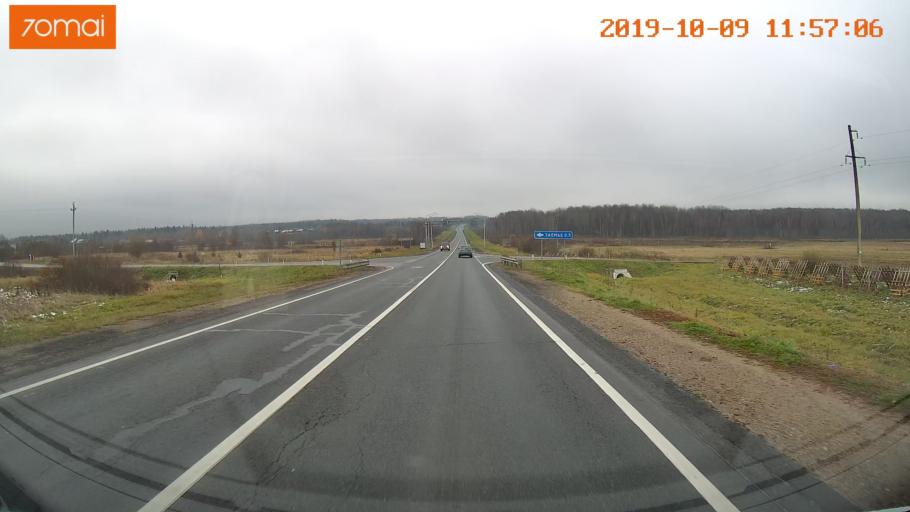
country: RU
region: Vologda
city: Gryazovets
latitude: 58.7366
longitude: 40.2907
